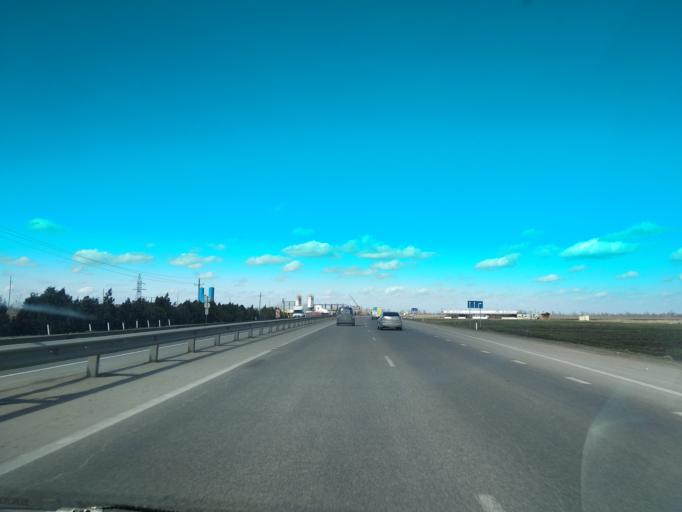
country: RU
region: Krasnodarskiy
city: Agronom
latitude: 45.1195
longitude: 39.1127
